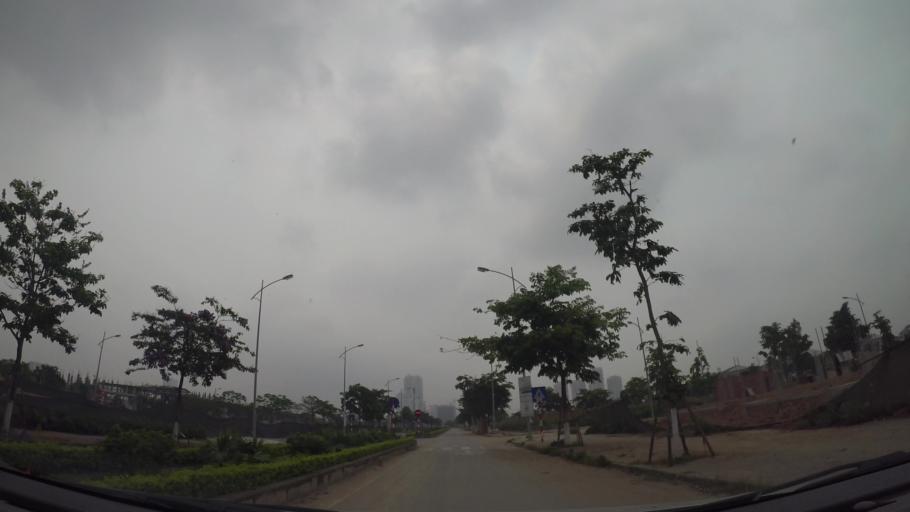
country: VN
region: Ha Noi
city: Ha Dong
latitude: 20.9852
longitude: 105.7523
